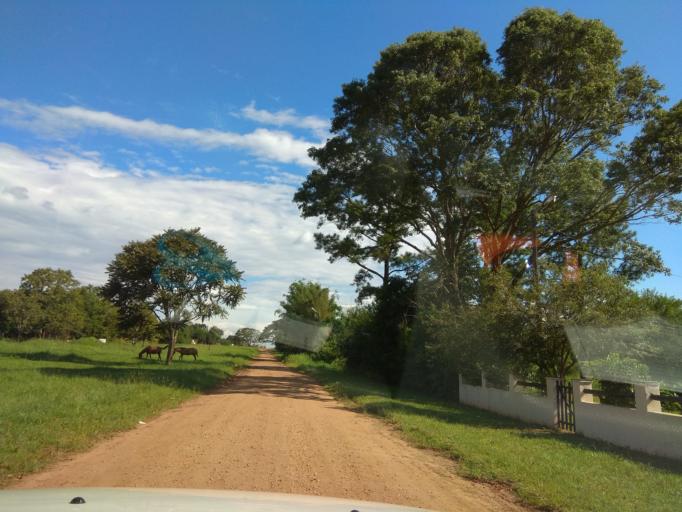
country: AR
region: Misiones
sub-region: Departamento de Candelaria
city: Candelaria
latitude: -27.4571
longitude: -55.7549
